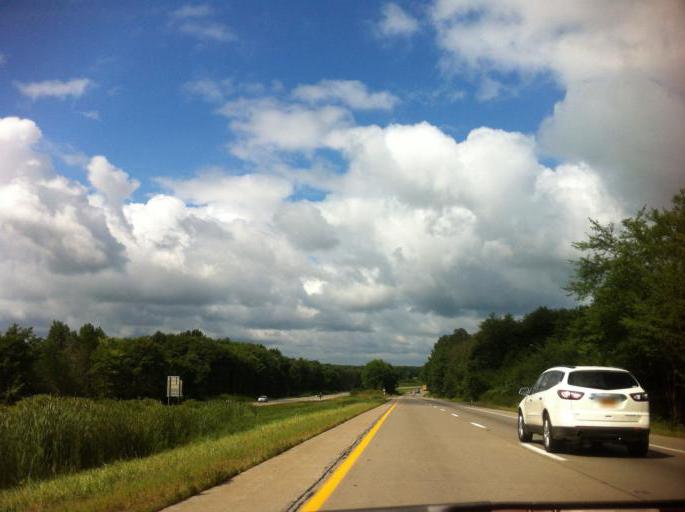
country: US
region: Pennsylvania
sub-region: Mercer County
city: Mercer
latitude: 41.1863
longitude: -80.2782
